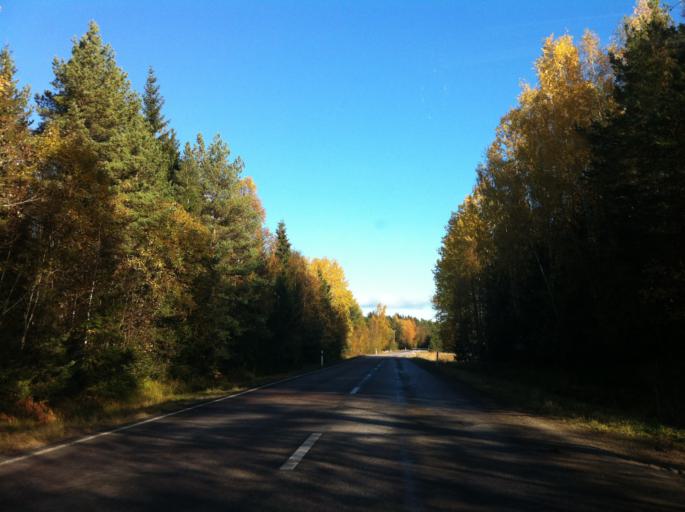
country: SE
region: Uppsala
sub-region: Osthammars Kommun
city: Oregrund
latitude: 60.3296
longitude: 18.3709
